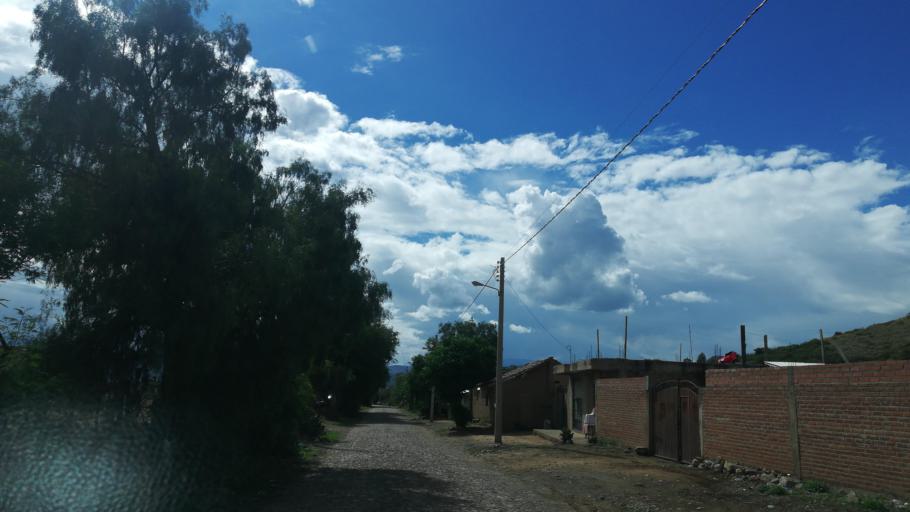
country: BO
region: Cochabamba
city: Capinota
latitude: -17.5498
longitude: -66.2247
